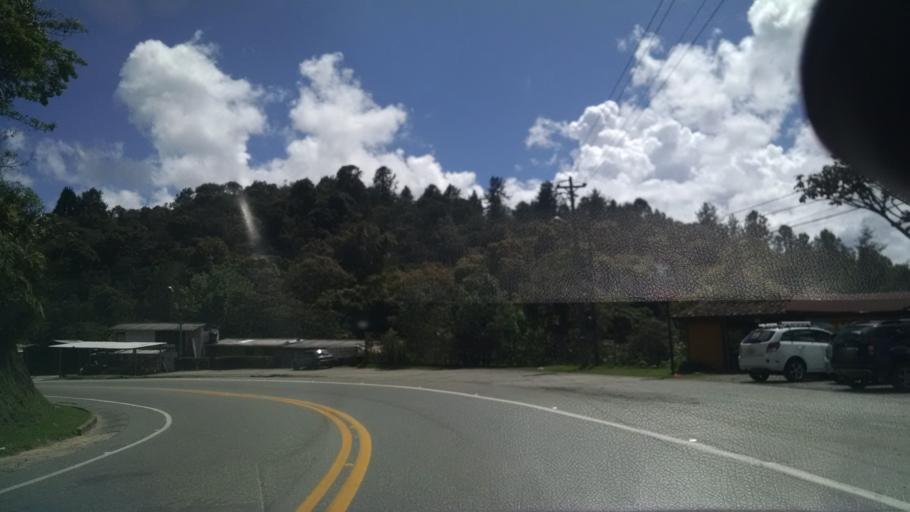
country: CO
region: Antioquia
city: Envigado
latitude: 6.1456
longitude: -75.5270
